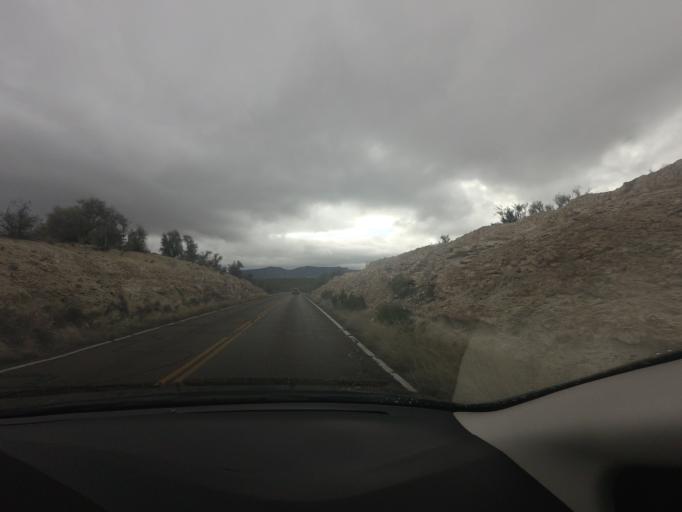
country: US
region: Arizona
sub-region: Yavapai County
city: Camp Verde
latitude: 34.6130
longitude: -111.8482
